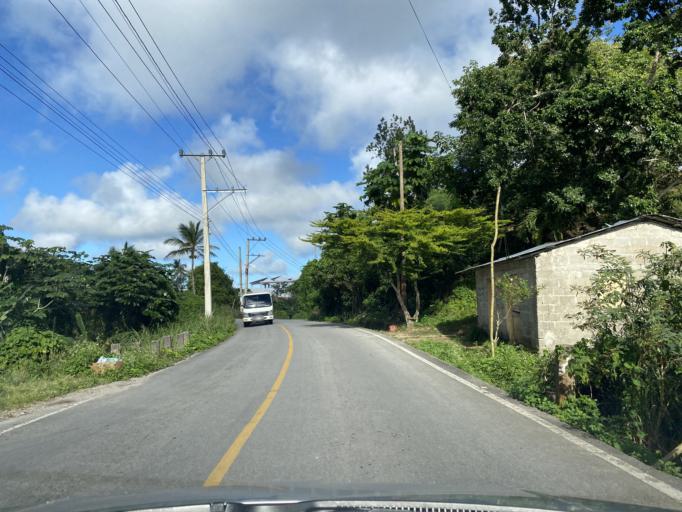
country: DO
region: Samana
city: Las Terrenas
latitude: 19.2614
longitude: -69.5677
